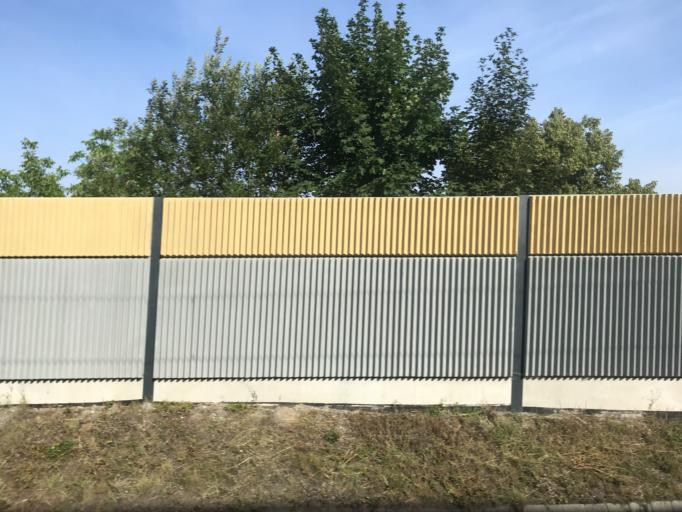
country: CZ
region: Jihocesky
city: Chotoviny
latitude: 49.5062
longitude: 14.6585
